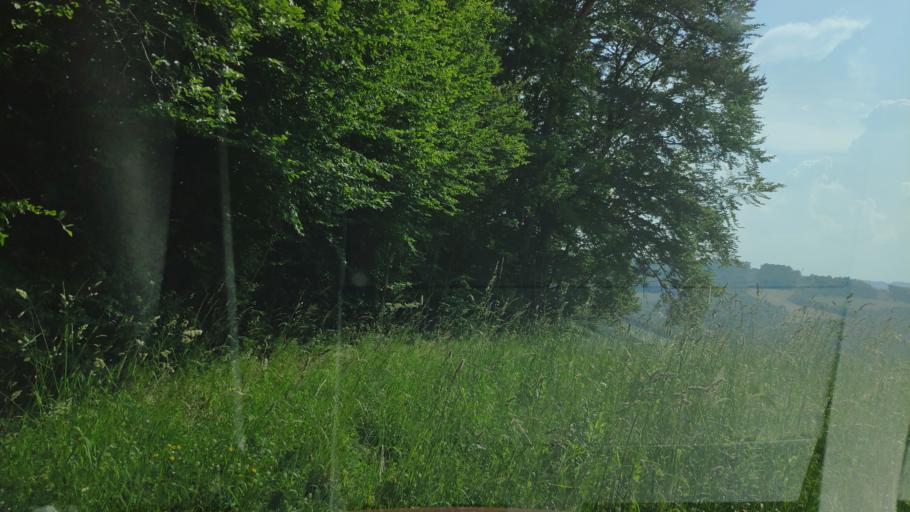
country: SK
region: Presovsky
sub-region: Okres Presov
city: Presov
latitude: 48.9661
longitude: 21.1525
